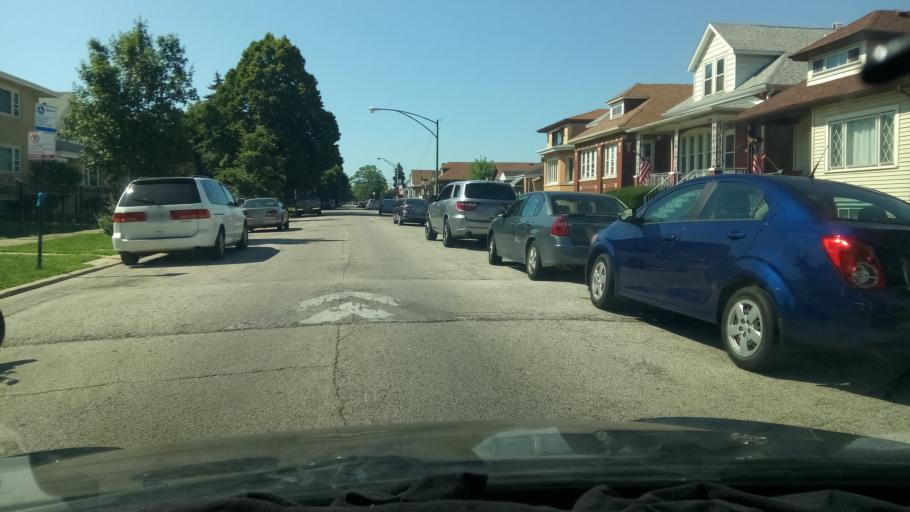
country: US
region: Illinois
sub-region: Cook County
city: Hometown
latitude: 41.7812
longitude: -87.7412
